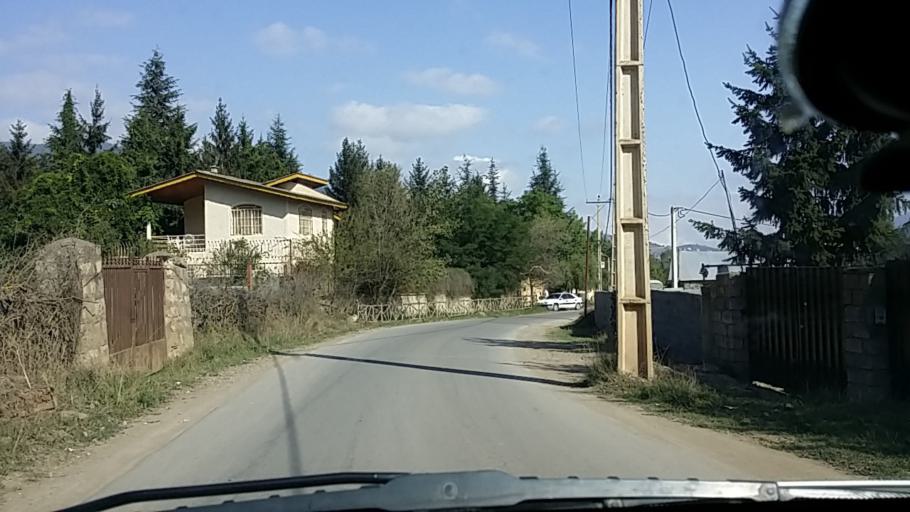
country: IR
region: Mazandaran
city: `Abbasabad
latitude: 36.5033
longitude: 51.1726
